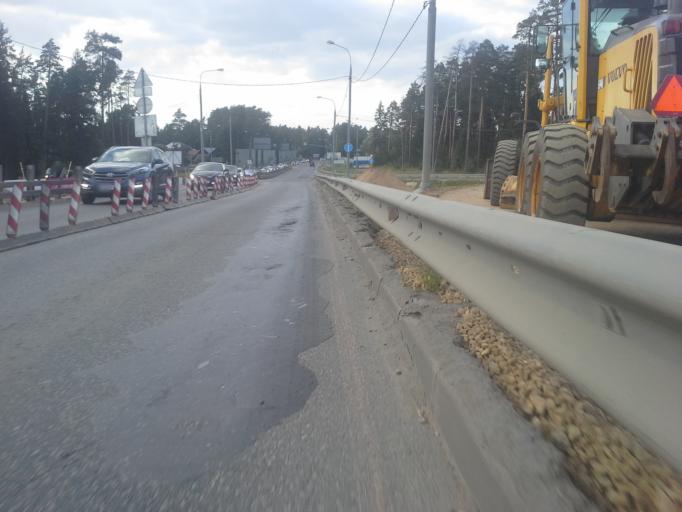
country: RU
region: Moskovskaya
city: Golitsyno
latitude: 55.6049
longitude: 37.0042
